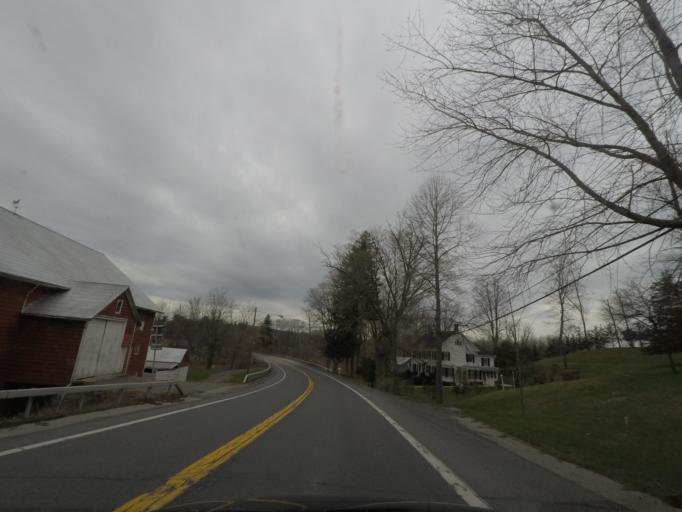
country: US
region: New York
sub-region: Albany County
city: Ravena
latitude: 42.5389
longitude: -73.8264
